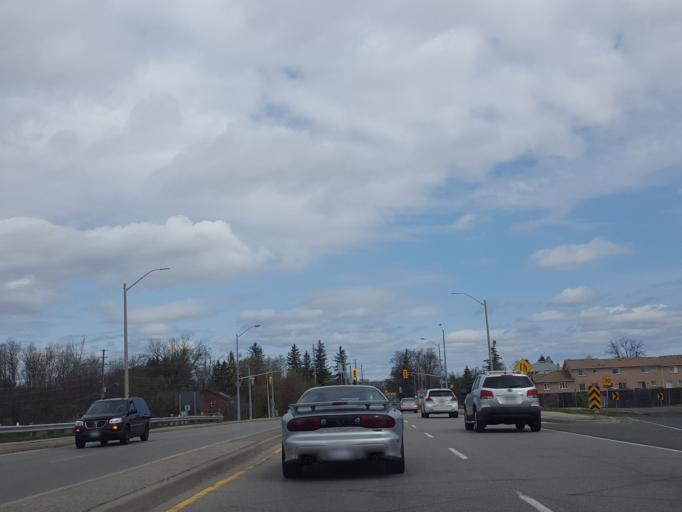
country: CA
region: Ontario
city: Markham
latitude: 43.8642
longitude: -79.2575
